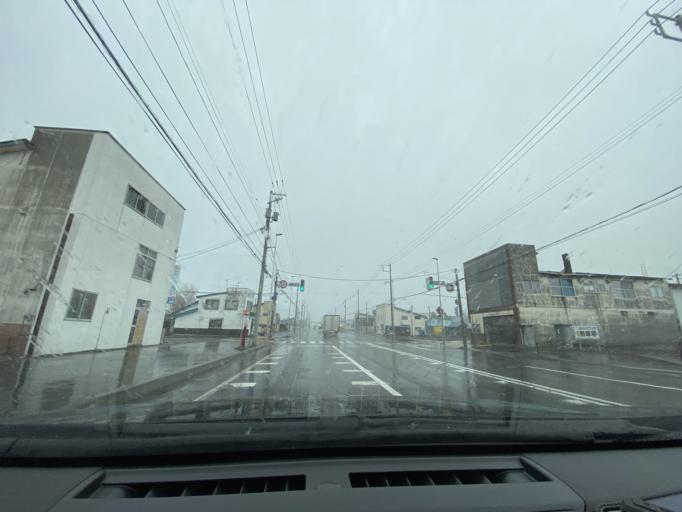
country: JP
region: Hokkaido
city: Takikawa
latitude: 43.6264
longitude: 141.9416
